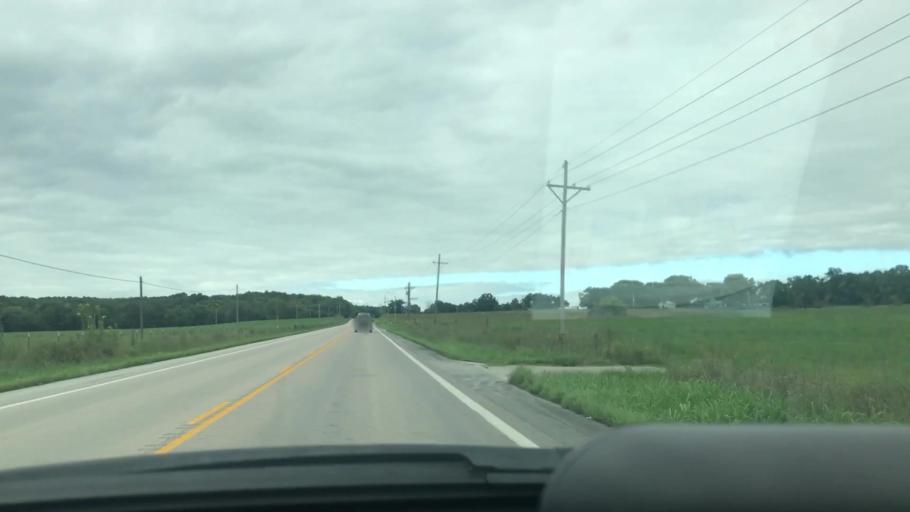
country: US
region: Missouri
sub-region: Hickory County
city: Hermitage
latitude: 37.8636
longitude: -93.1784
